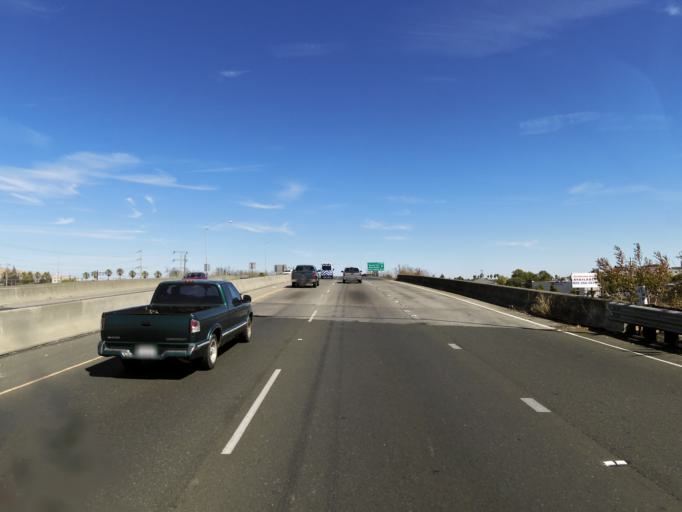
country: US
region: California
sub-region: Solano County
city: Suisun
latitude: 38.2429
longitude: -122.0438
